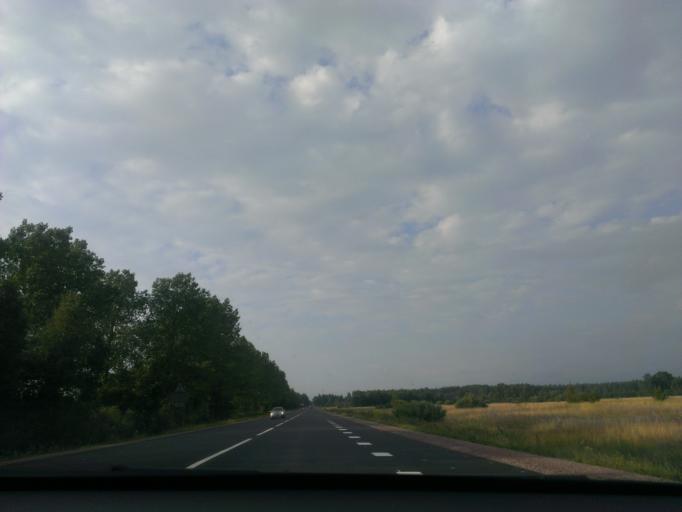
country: LV
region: Lecava
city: Iecava
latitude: 56.6834
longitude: 24.2389
